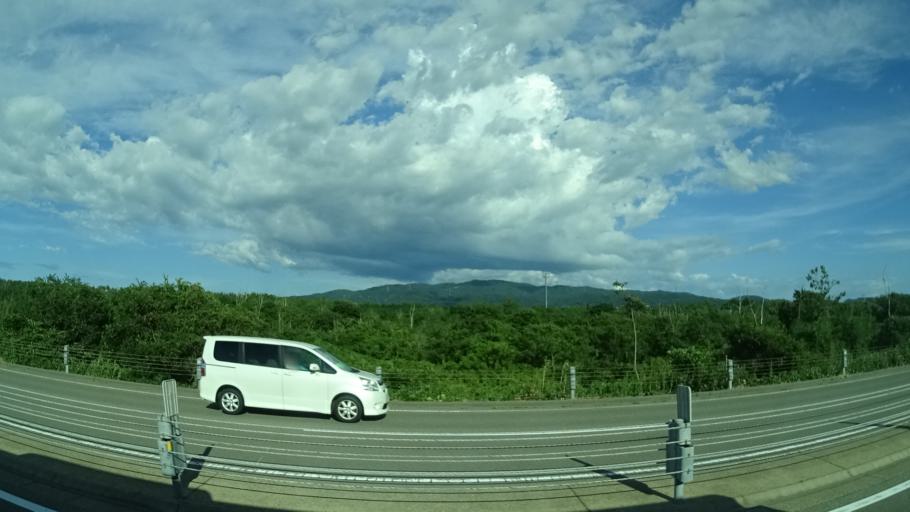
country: JP
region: Ishikawa
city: Hakui
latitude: 36.8087
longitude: 136.7371
